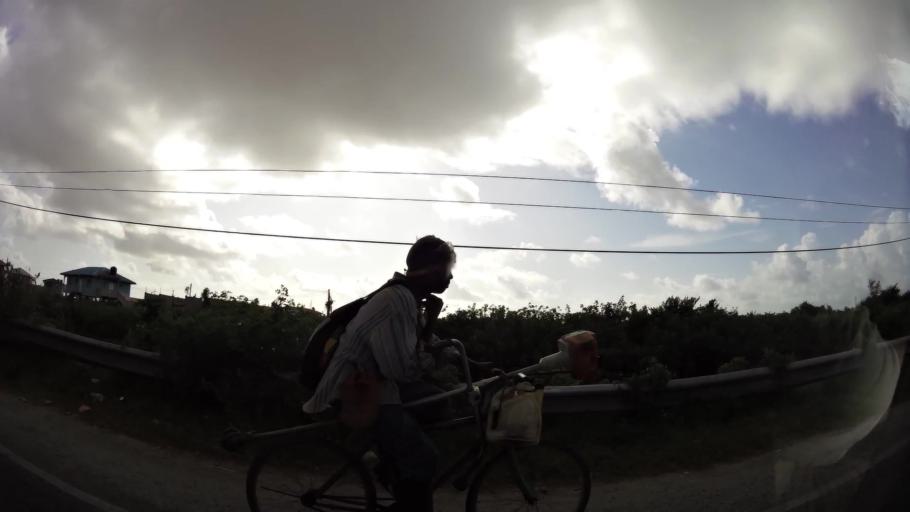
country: GY
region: Demerara-Mahaica
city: Mahaica Village
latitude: 6.7842
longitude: -58.0112
